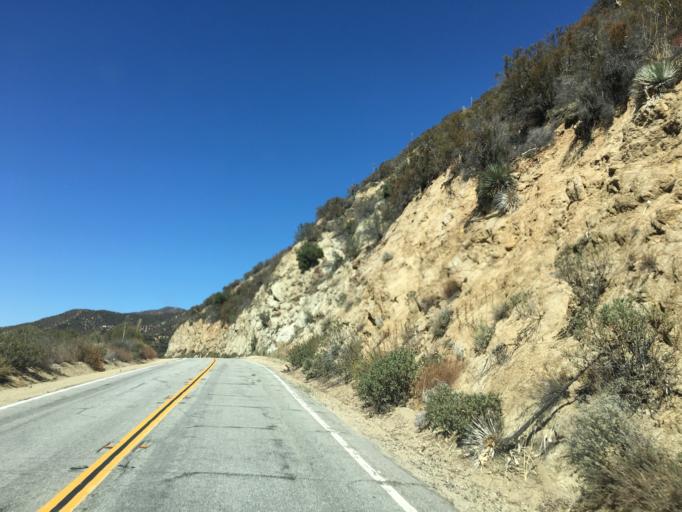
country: US
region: California
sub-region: Los Angeles County
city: Green Valley
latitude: 34.6322
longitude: -118.5366
